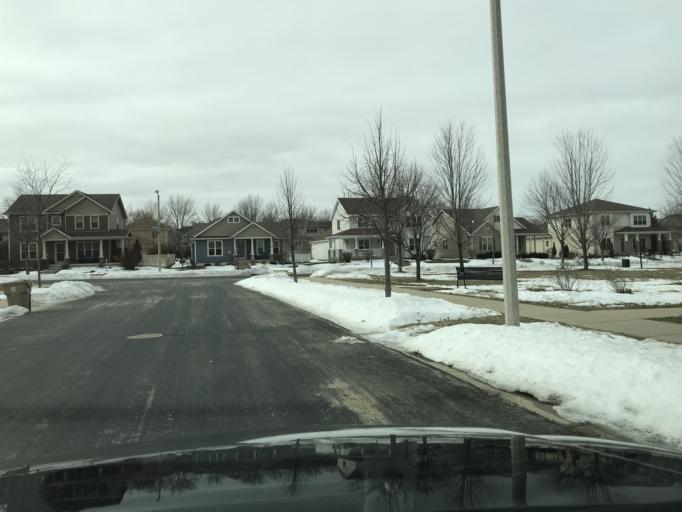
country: US
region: Wisconsin
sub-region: Dane County
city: Monona
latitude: 43.0885
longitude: -89.2737
